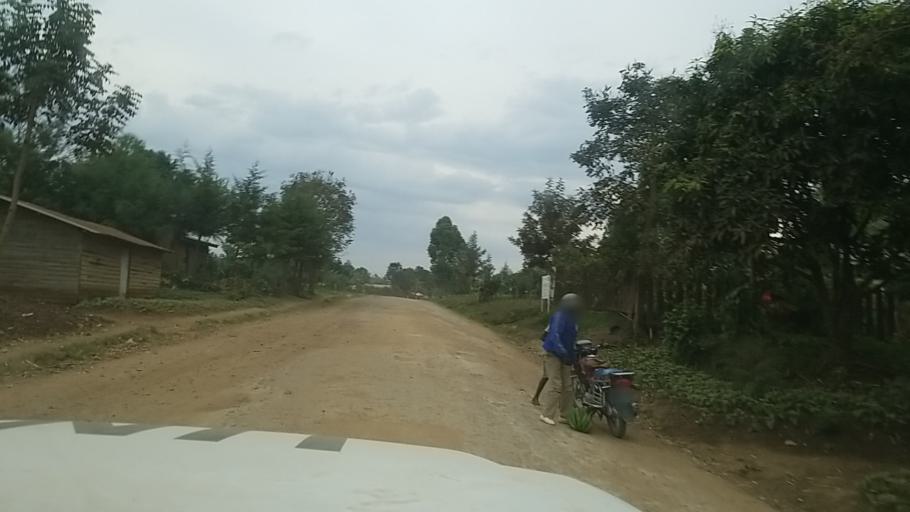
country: CD
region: South Kivu
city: Bukavu
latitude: -2.2671
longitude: 28.8199
